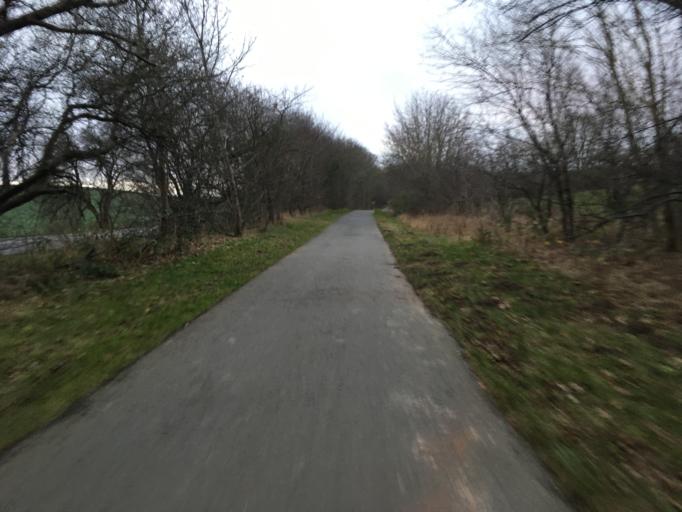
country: DE
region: Mecklenburg-Vorpommern
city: Sassnitz
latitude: 54.5086
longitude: 13.5982
